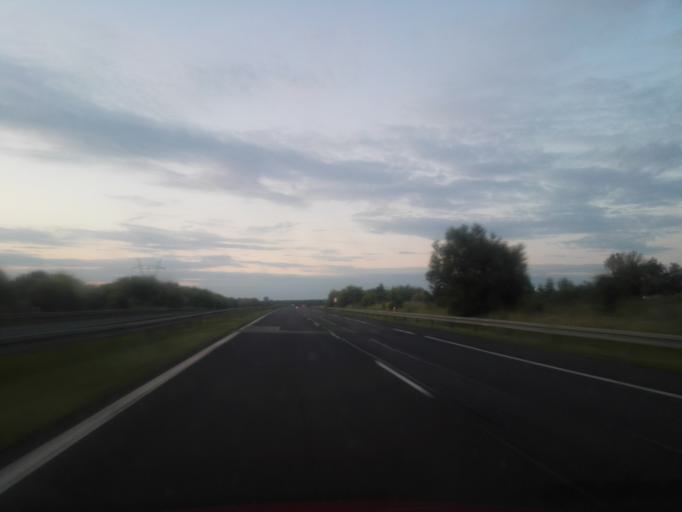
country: PL
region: Lodz Voivodeship
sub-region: Powiat piotrkowski
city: Wola Krzysztoporska
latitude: 51.2895
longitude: 19.5414
